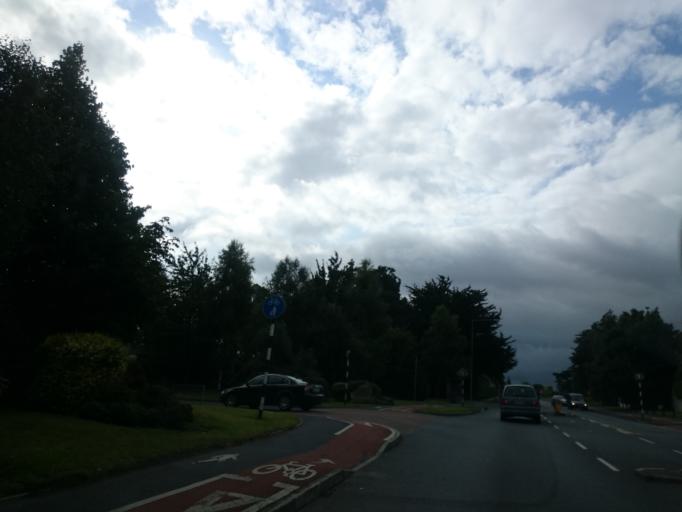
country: IE
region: Leinster
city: Mount Merrion
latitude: 53.2907
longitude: -6.2278
